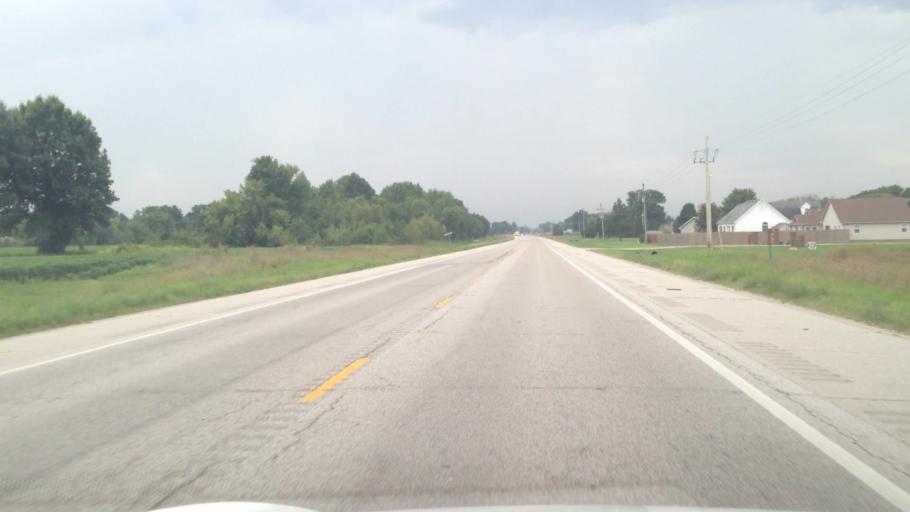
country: US
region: Kansas
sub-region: Cherokee County
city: Galena
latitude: 37.0967
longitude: -94.7045
